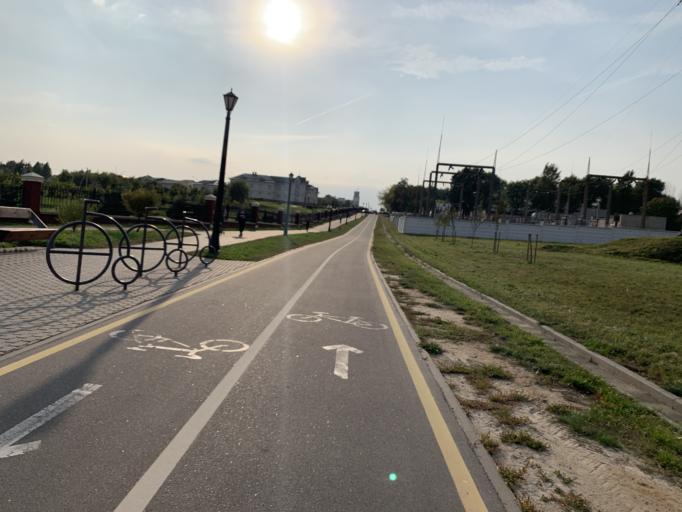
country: BY
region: Minsk
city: Minsk
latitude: 53.8604
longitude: 27.5804
